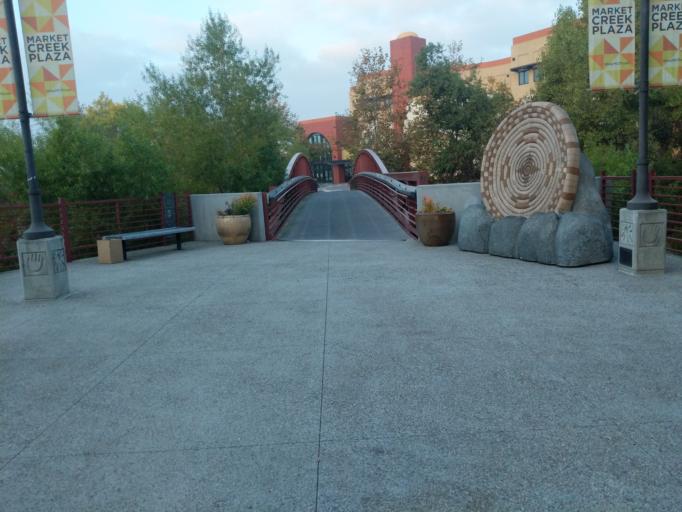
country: US
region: California
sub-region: San Diego County
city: National City
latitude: 32.7088
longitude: -117.0868
